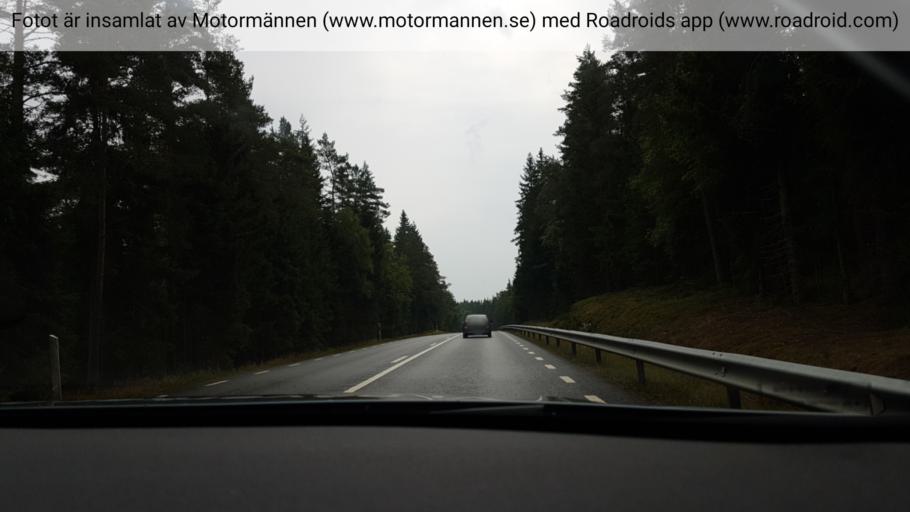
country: SE
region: Joenkoeping
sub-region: Savsjo Kommun
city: Vrigstad
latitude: 57.3806
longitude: 14.4025
